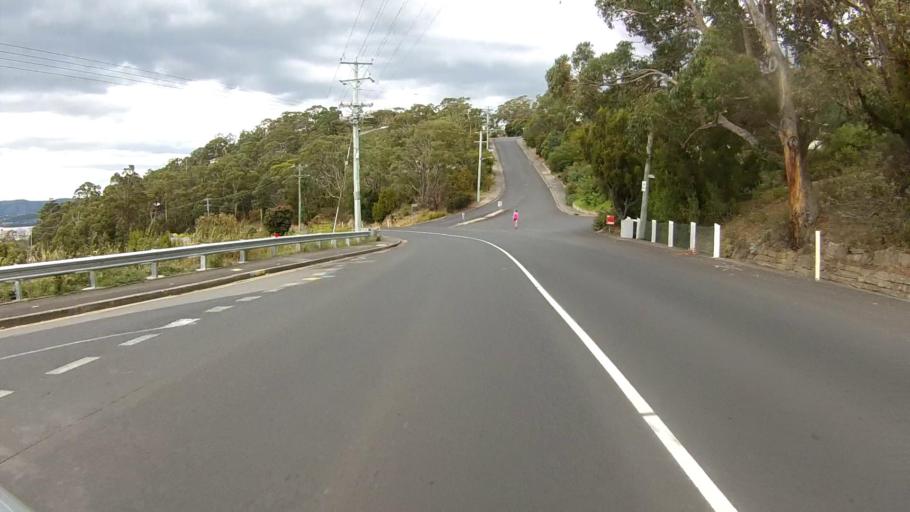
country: AU
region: Tasmania
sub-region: Hobart
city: Dynnyrne
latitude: -42.9004
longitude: 147.2972
